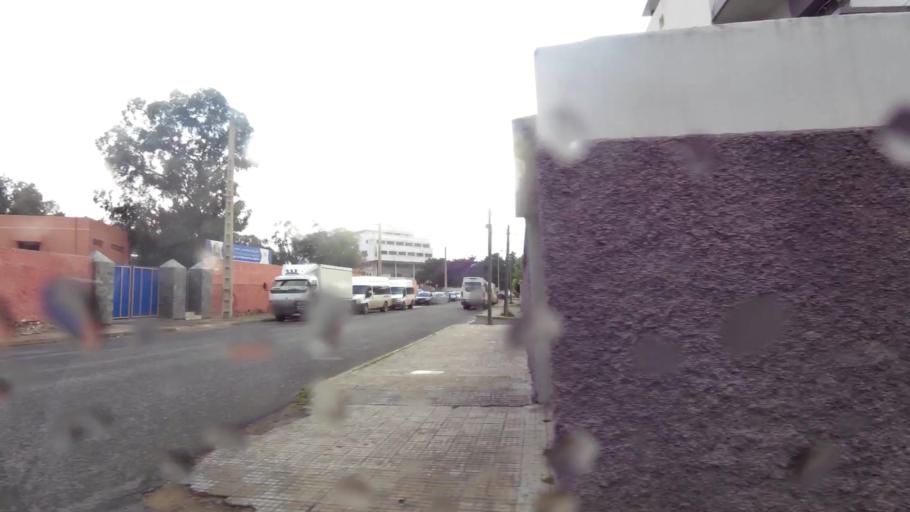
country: MA
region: Doukkala-Abda
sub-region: El-Jadida
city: El Jadida
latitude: 33.2427
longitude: -8.5020
